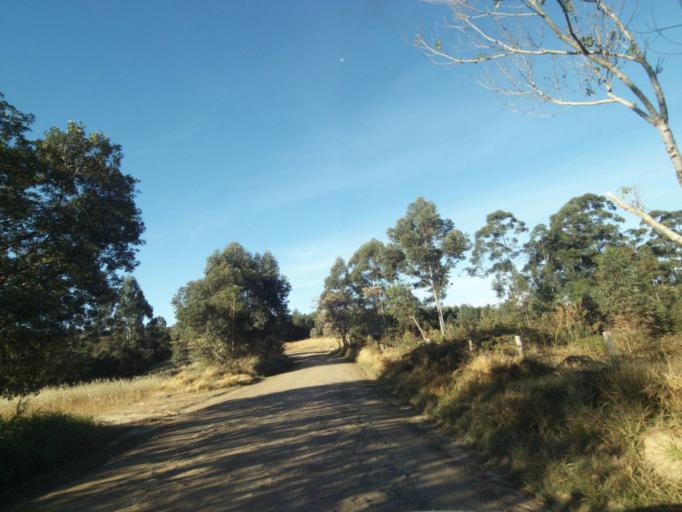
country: BR
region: Parana
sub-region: Tibagi
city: Tibagi
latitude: -24.5289
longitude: -50.5958
